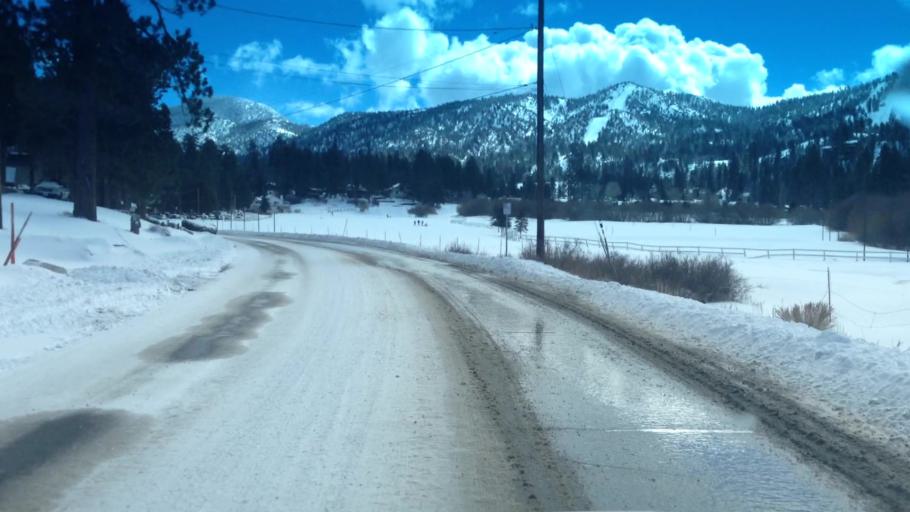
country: US
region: California
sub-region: San Bernardino County
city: Big Bear City
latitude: 34.2388
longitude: -116.8660
